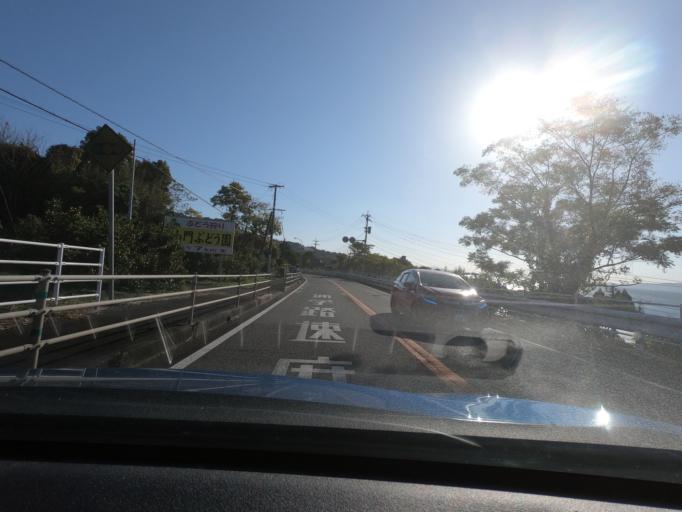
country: JP
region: Kumamoto
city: Minamata
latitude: 32.1568
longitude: 130.3636
